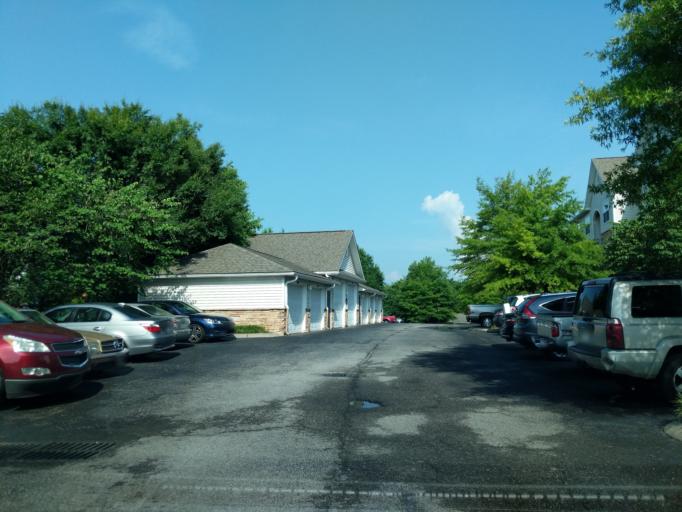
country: US
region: Tennessee
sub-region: Sumner County
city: Hendersonville
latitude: 36.3120
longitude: -86.6595
